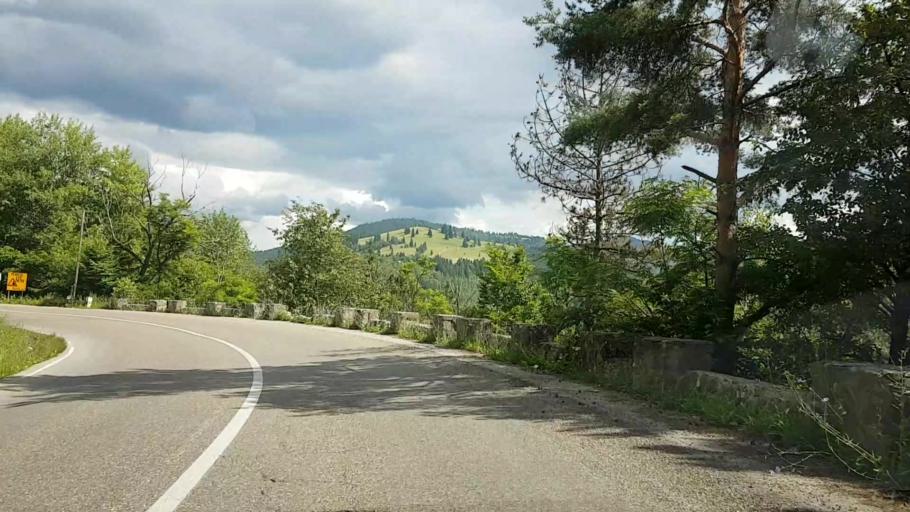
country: RO
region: Neamt
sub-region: Comuna Ceahlau
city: Ceahlau
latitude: 47.0531
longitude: 25.9790
